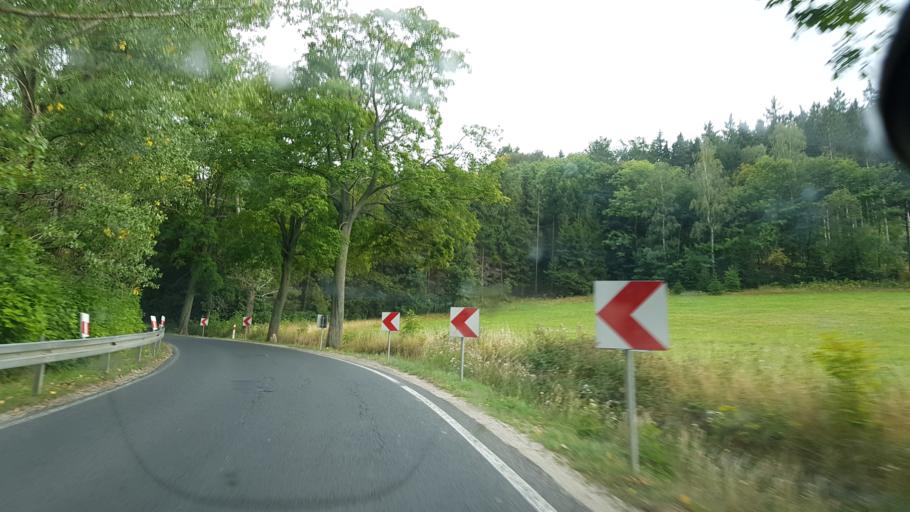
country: PL
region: Lower Silesian Voivodeship
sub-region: Powiat jeleniogorski
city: Janowice Wielkie
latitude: 50.8989
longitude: 15.9747
